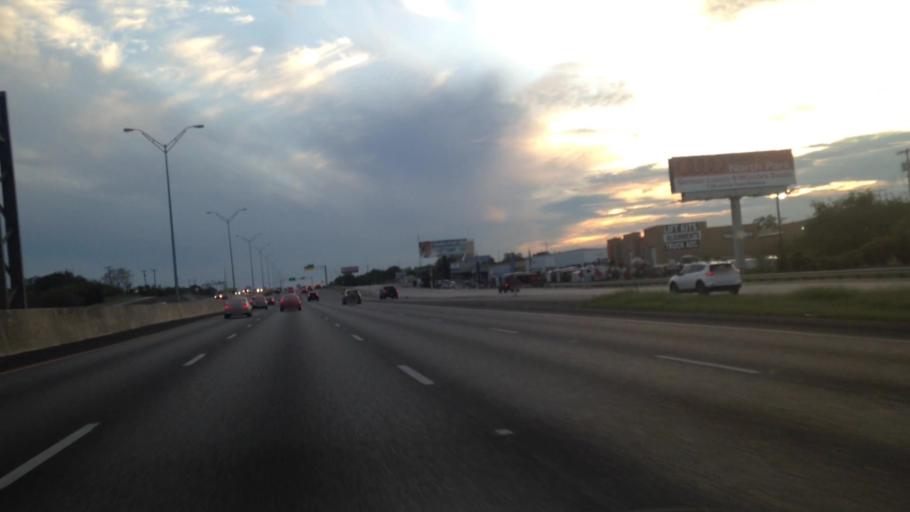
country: US
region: Texas
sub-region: Comal County
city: New Braunfels
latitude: 29.6721
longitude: -98.1587
